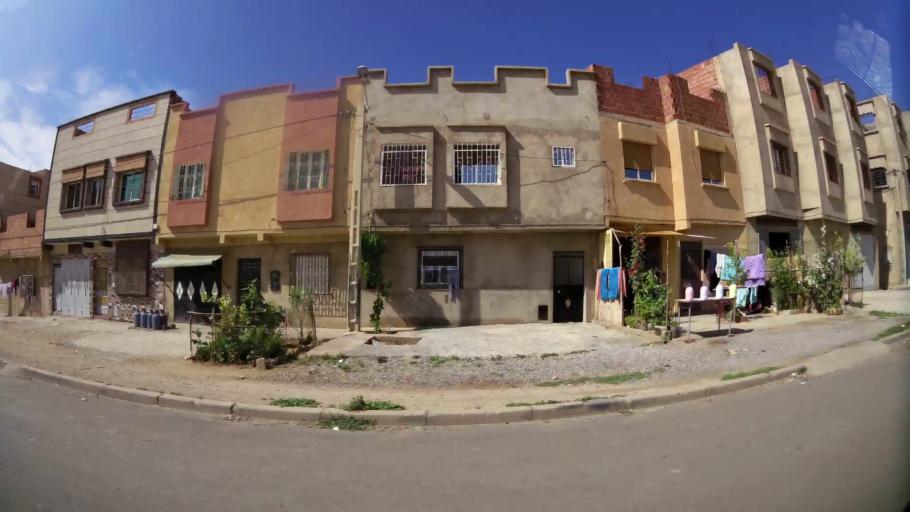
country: MA
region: Oriental
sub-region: Oujda-Angad
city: Oujda
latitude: 34.6984
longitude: -1.8711
